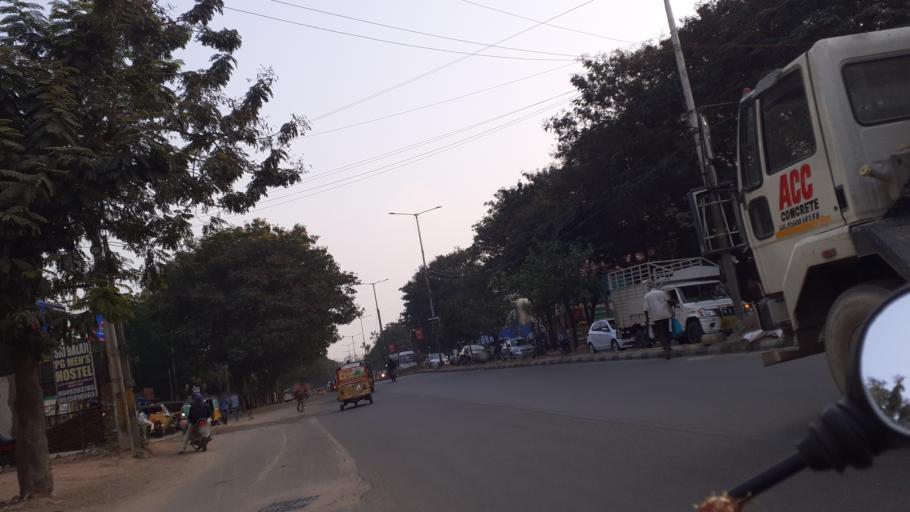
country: IN
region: Telangana
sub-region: Rangareddi
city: Kukatpalli
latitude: 17.4742
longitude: 78.3639
